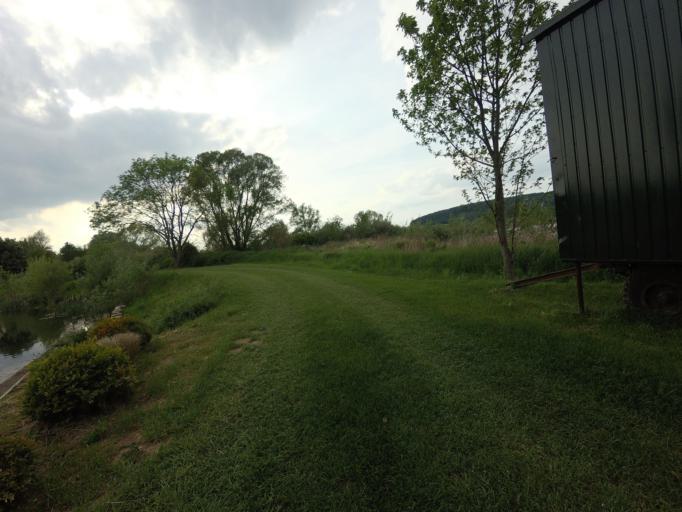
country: DE
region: Lower Saxony
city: Nordstemmen
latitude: 52.1598
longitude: 9.7593
